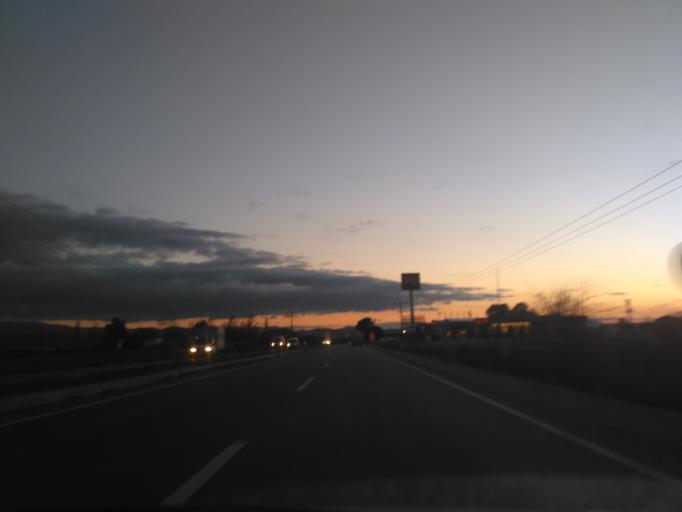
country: TR
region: Balikesir
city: Burhaniye
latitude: 39.5344
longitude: 27.0089
